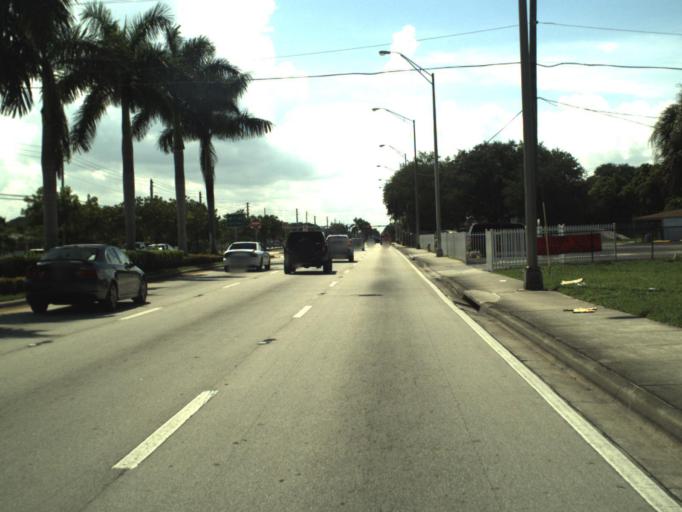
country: US
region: Florida
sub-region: Miami-Dade County
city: Scott Lake
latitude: 25.9418
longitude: -80.2261
